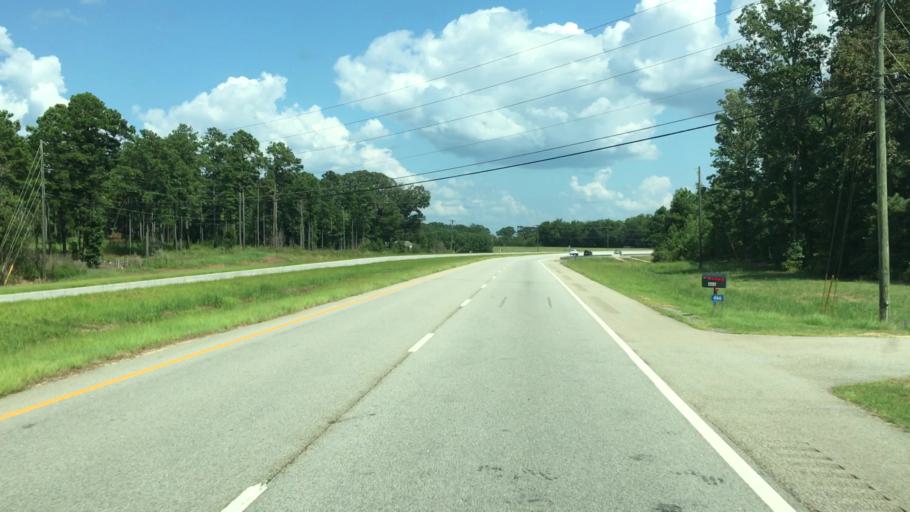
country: US
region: Georgia
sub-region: Putnam County
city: Eatonton
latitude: 33.2697
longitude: -83.3409
